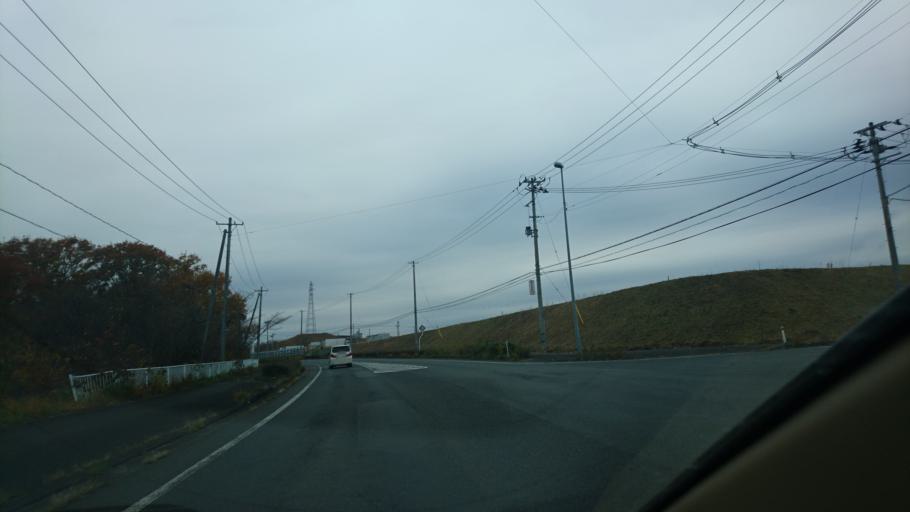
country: JP
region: Iwate
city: Kitakami
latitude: 39.2374
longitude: 141.0922
